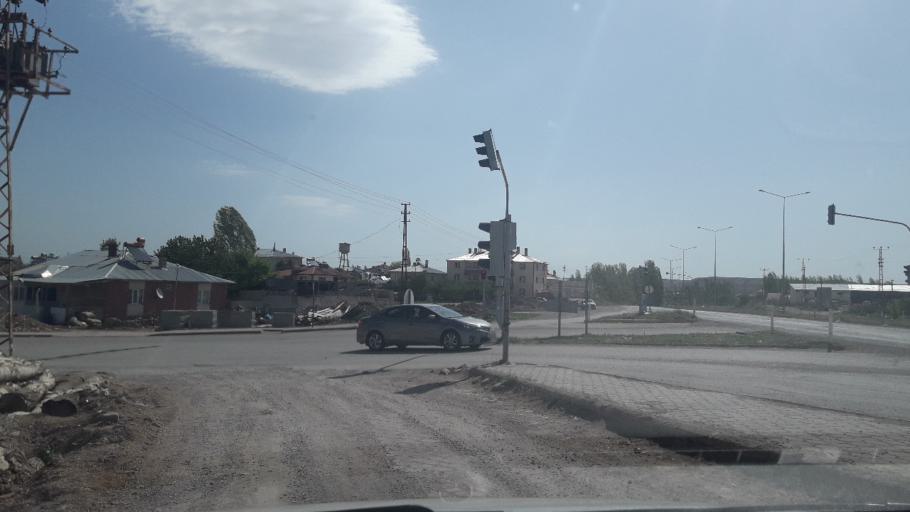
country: TR
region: Sivas
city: Kangal
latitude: 39.2293
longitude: 37.3882
